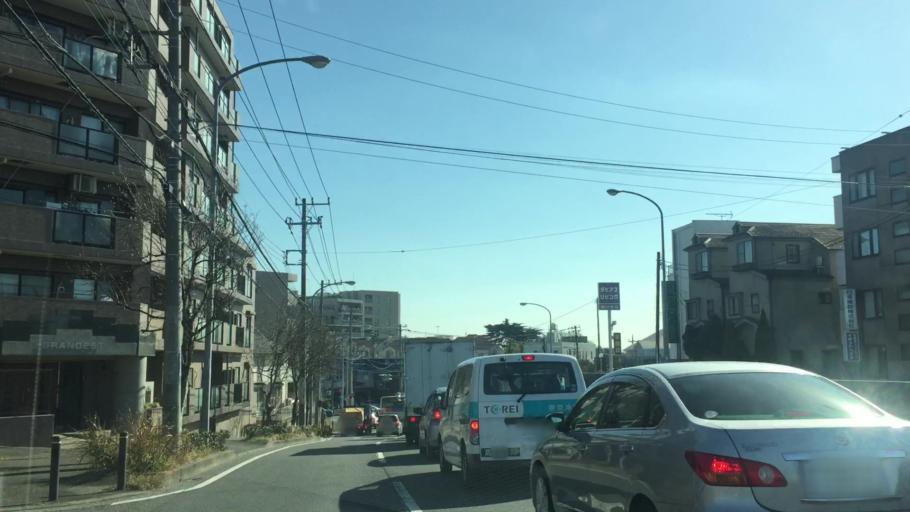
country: JP
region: Kanagawa
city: Yokohama
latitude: 35.4815
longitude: 139.6003
